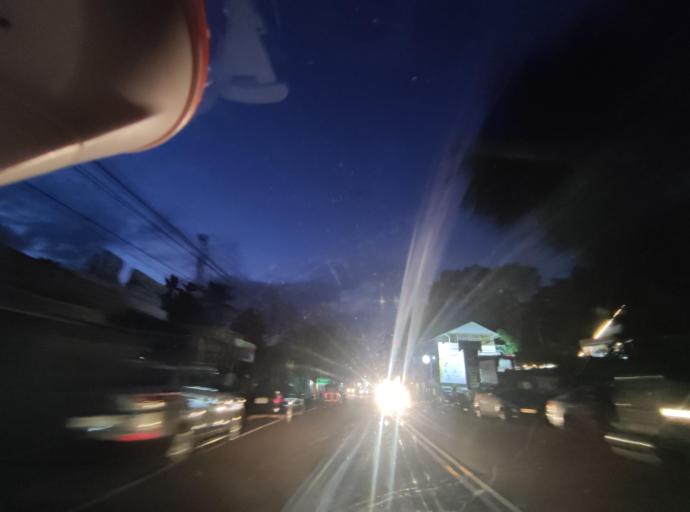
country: IN
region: Kerala
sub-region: Thiruvananthapuram
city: Thiruvananthapuram
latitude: 8.5491
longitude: 76.9607
